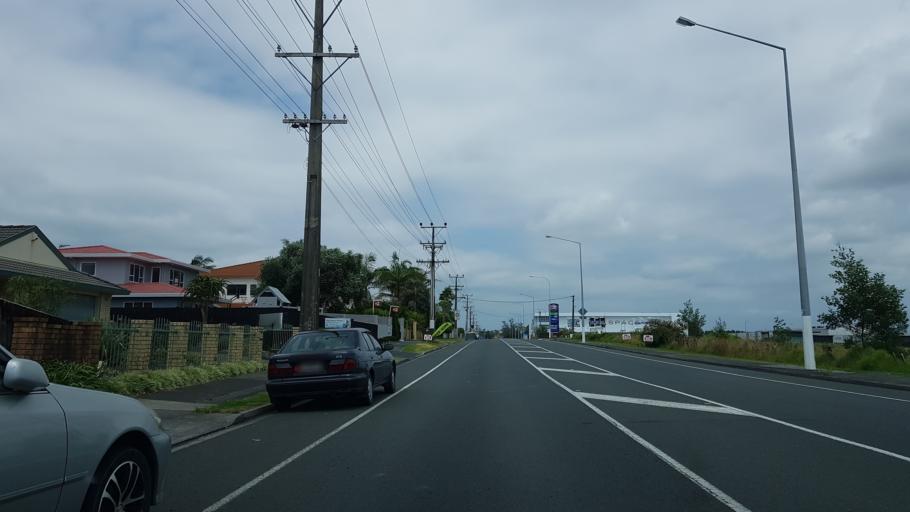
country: NZ
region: Auckland
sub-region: Auckland
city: Rosebank
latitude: -36.8019
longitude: 174.6403
